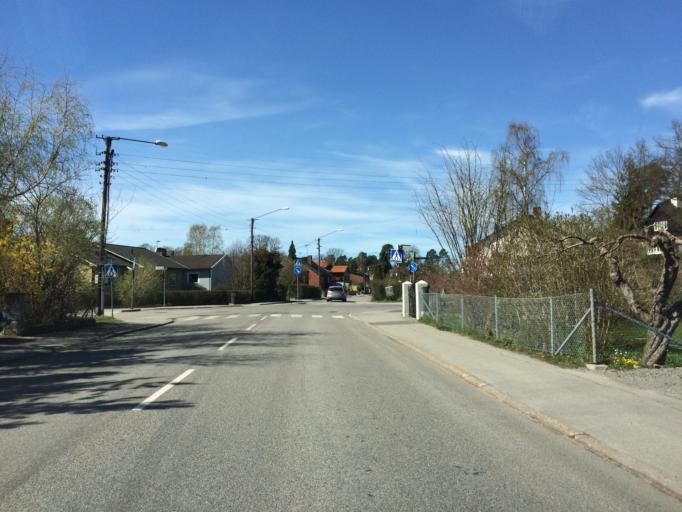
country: SE
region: Stockholm
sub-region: Huddinge Kommun
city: Huddinge
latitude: 59.2667
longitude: 17.9776
